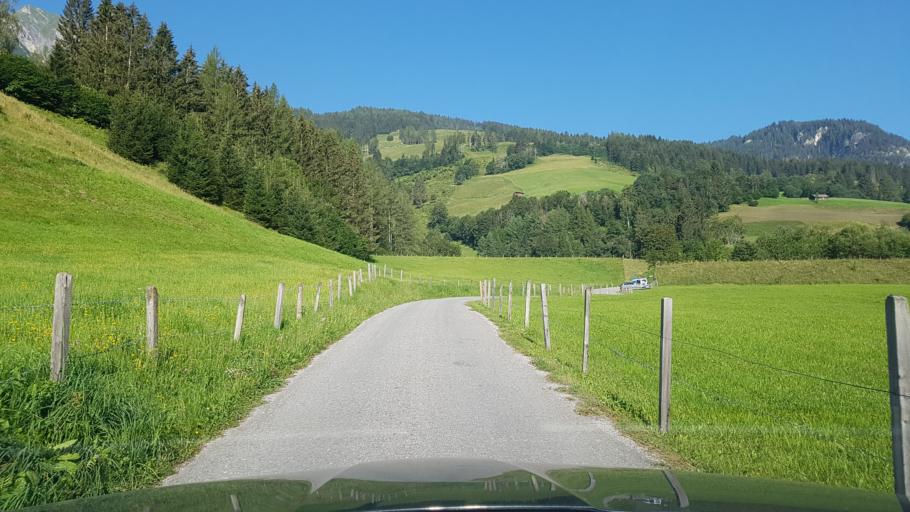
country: AT
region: Salzburg
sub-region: Politischer Bezirk Sankt Johann im Pongau
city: Dorfgastein
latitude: 47.2576
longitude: 13.0809
